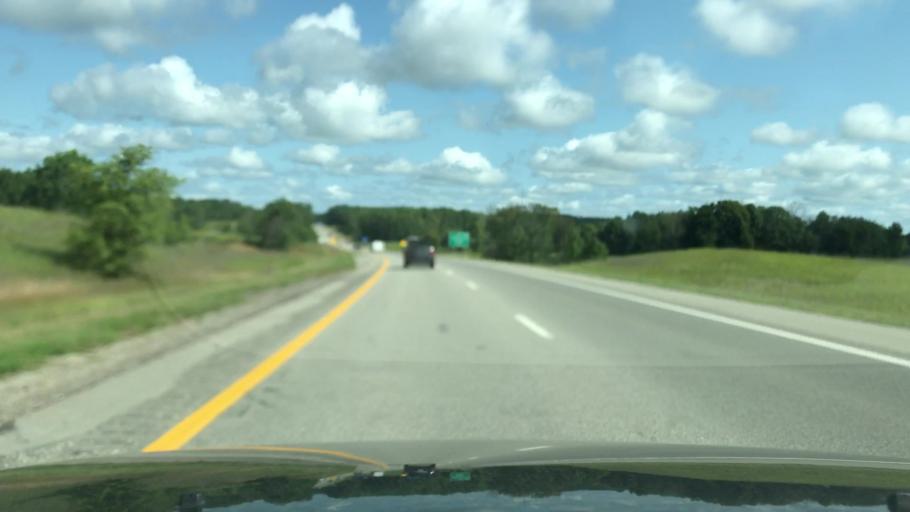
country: US
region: Michigan
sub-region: Montcalm County
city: Howard City
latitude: 43.4683
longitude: -85.4761
